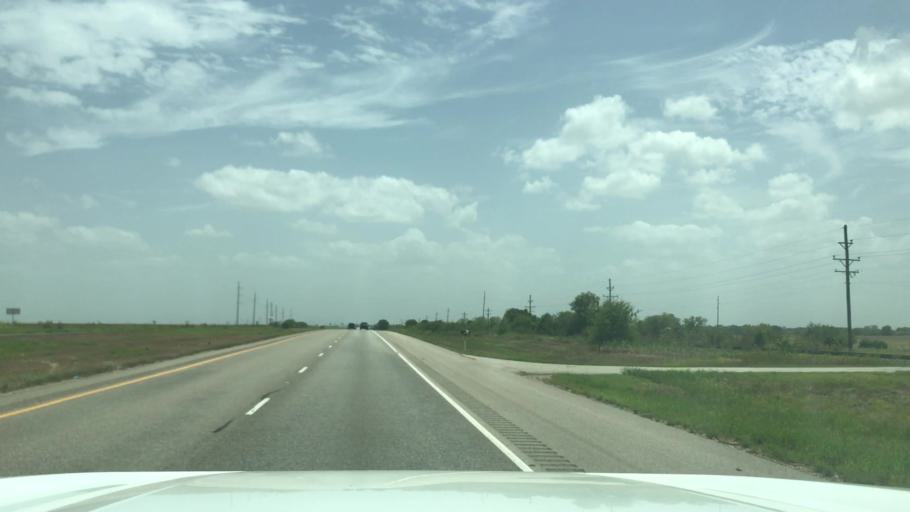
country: US
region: Texas
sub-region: Falls County
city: Marlin
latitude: 31.3421
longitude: -96.8933
